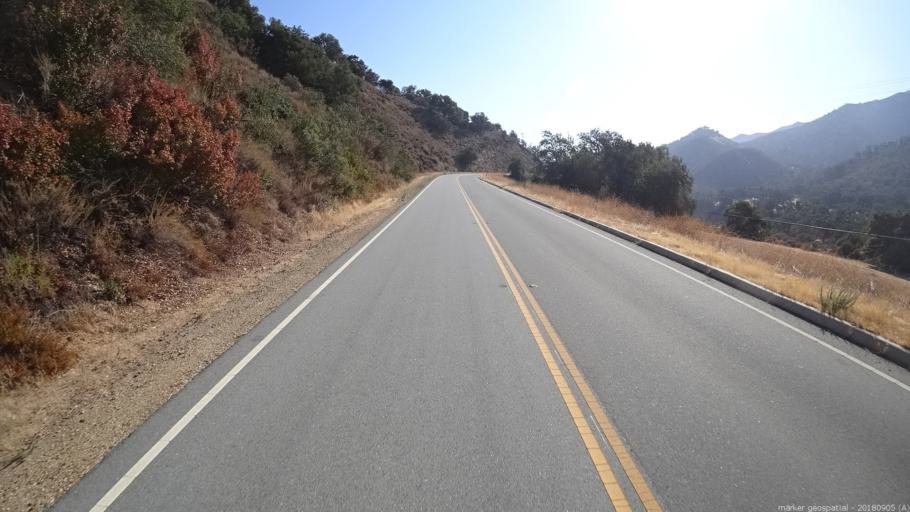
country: US
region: California
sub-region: Monterey County
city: Greenfield
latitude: 36.2322
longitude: -121.4619
